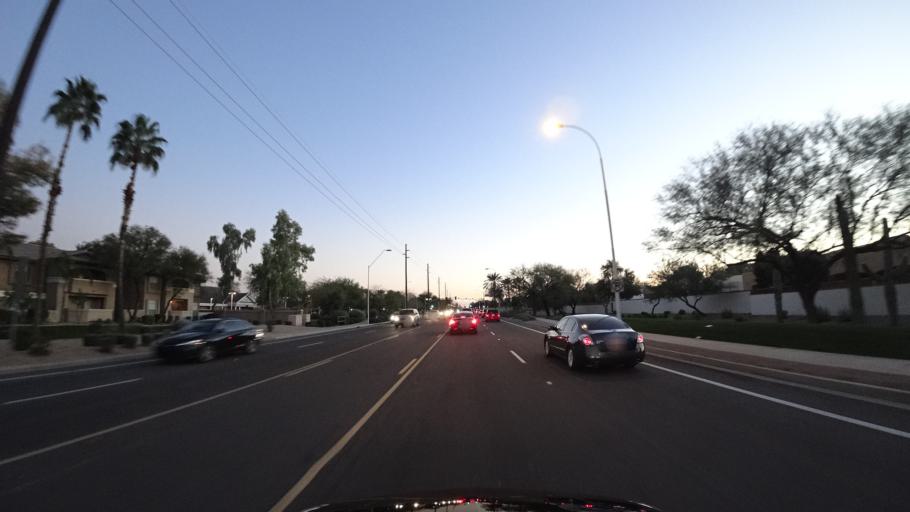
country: US
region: Arizona
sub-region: Maricopa County
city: Chandler
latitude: 33.3148
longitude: -111.8764
